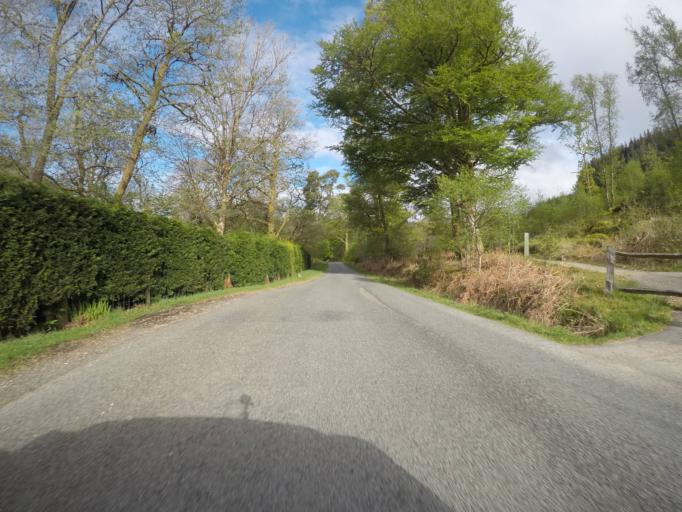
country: GB
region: Scotland
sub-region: Highland
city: Fort William
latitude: 56.6811
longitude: -5.0874
